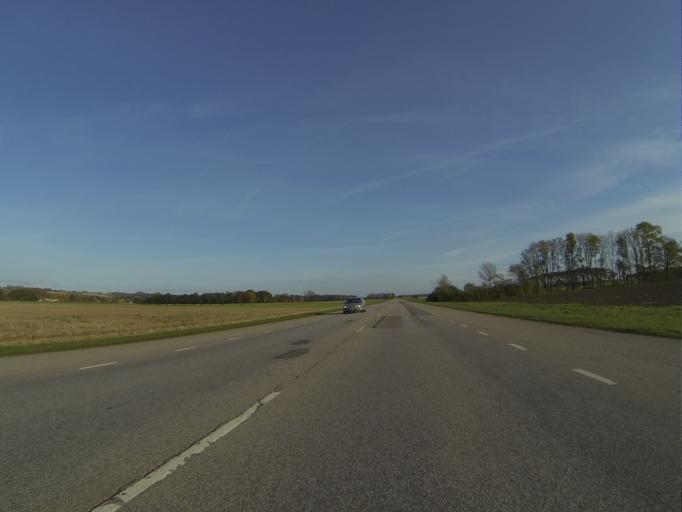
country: SE
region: Skane
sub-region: Hoors Kommun
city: Loberod
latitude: 55.7296
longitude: 13.4222
